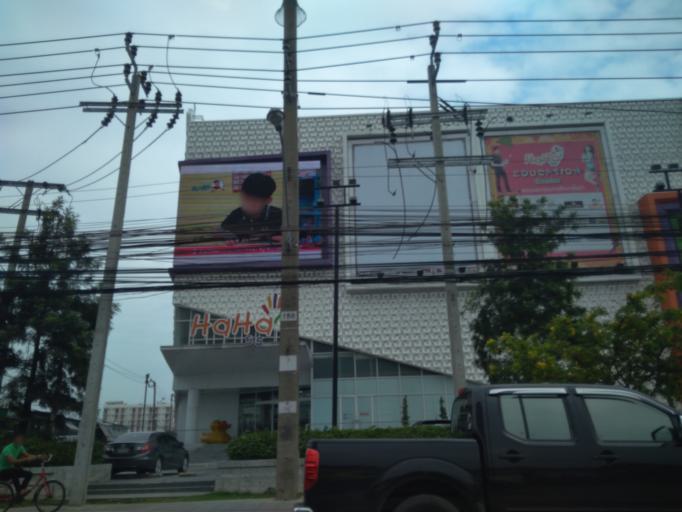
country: TH
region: Bangkok
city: Bang Na
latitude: 13.6904
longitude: 100.6471
